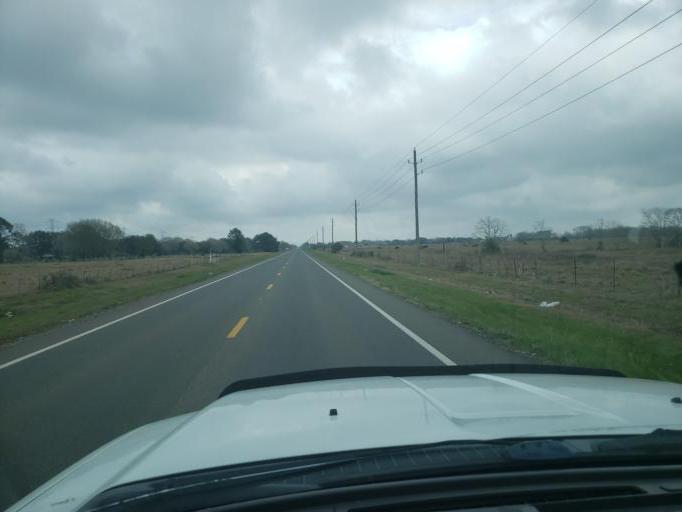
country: US
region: Texas
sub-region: Fort Bend County
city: Needville
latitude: 29.3645
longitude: -95.7612
